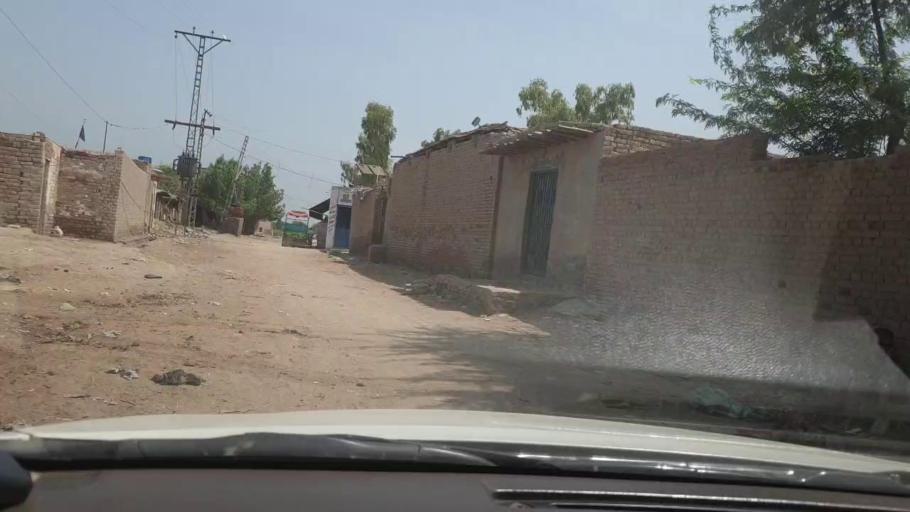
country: PK
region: Sindh
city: Shikarpur
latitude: 27.9334
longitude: 68.6025
